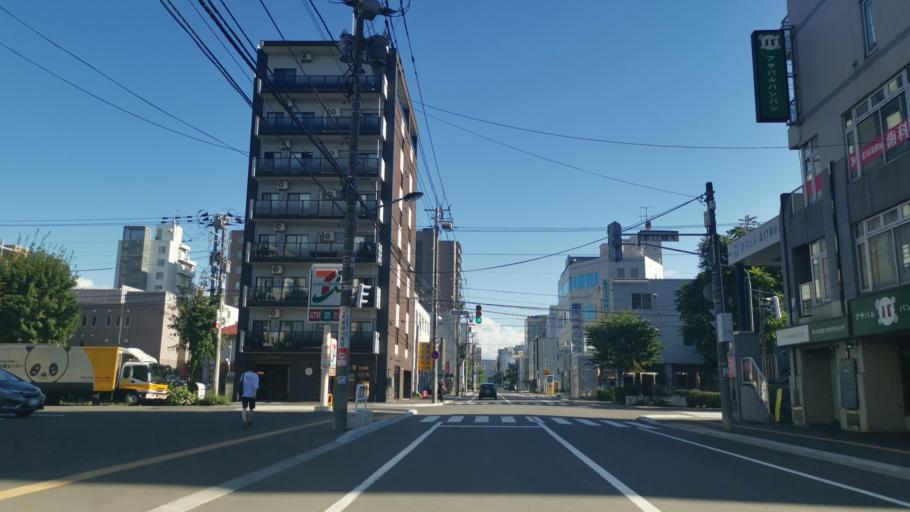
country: JP
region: Hokkaido
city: Sapporo
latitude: 43.0809
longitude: 141.3470
